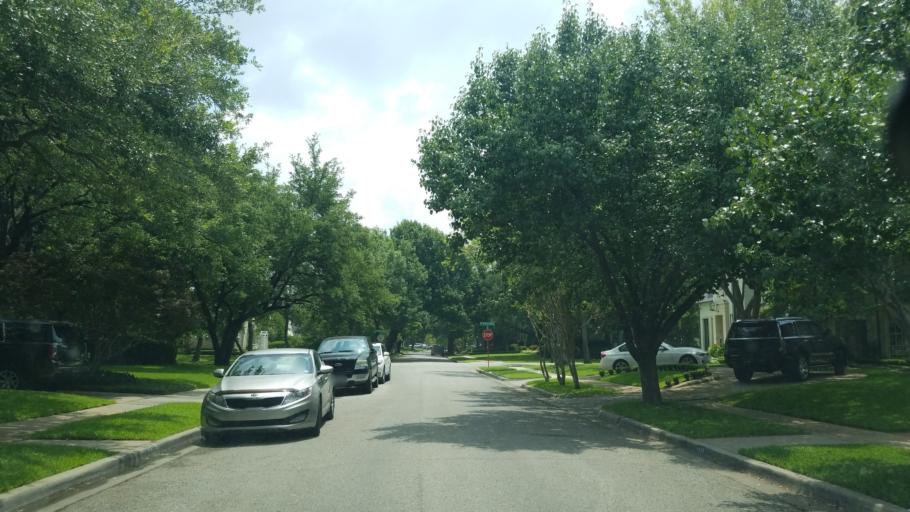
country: US
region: Texas
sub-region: Dallas County
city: University Park
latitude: 32.8388
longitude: -96.8119
